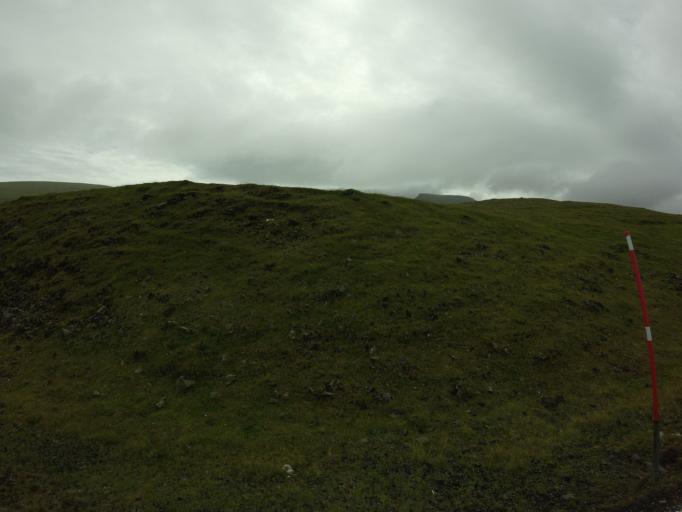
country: FO
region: Sandoy
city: Sandur
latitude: 61.8258
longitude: -6.6937
